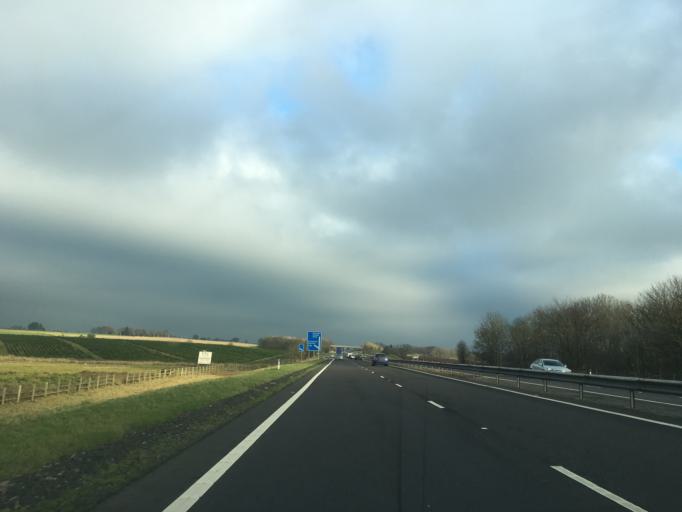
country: GB
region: Scotland
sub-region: Perth and Kinross
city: Milnathort
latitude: 56.2365
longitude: -3.3964
